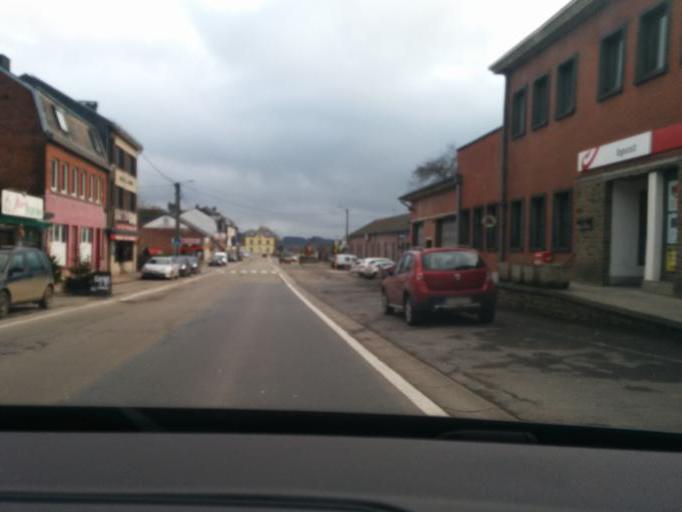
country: BE
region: Wallonia
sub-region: Province du Luxembourg
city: Gouvy
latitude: 50.1903
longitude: 5.9535
